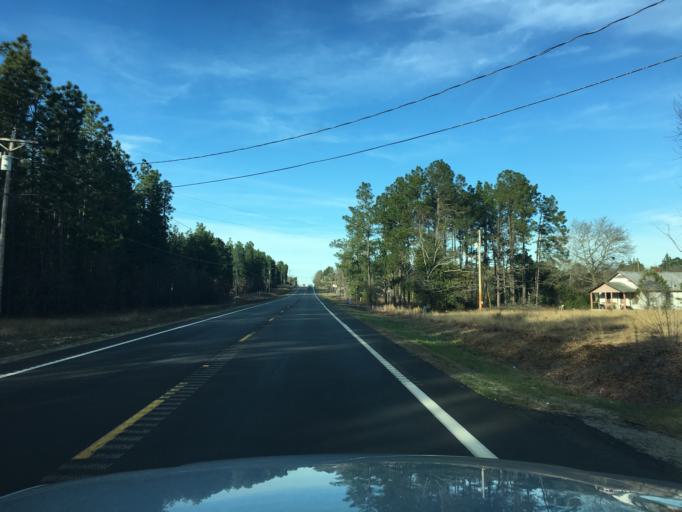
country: US
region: South Carolina
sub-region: Aiken County
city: Aiken
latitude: 33.6826
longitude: -81.6674
